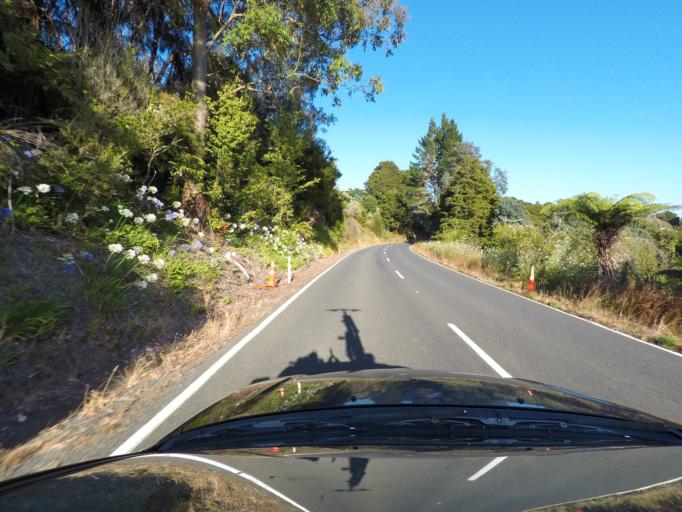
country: NZ
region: Northland
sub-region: Whangarei
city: Whangarei
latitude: -35.6644
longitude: 174.3192
